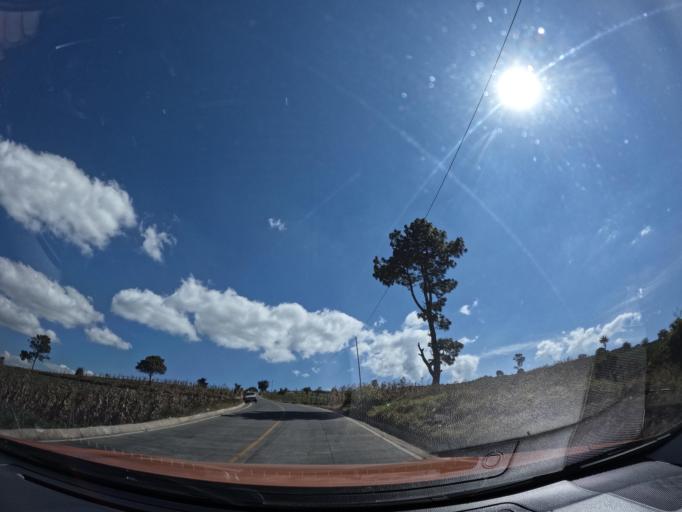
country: GT
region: Chimaltenango
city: Patzun
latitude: 14.6665
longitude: -91.0568
